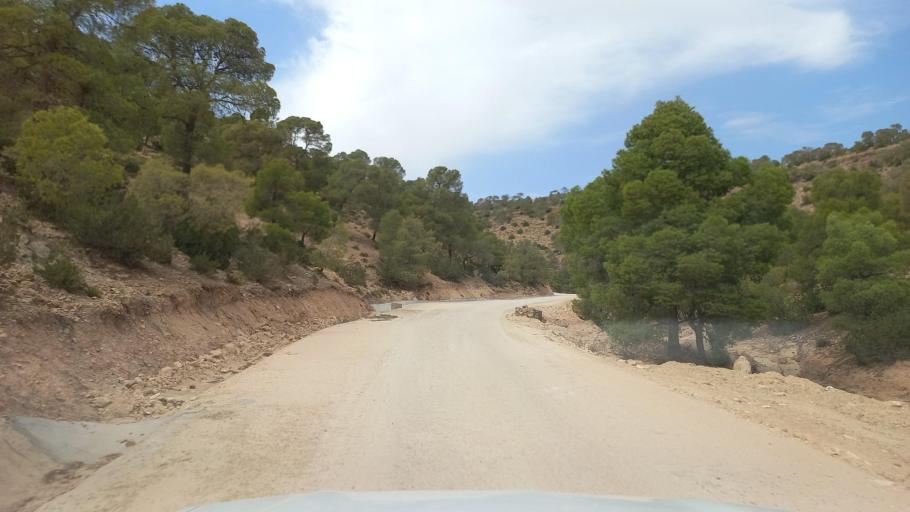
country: TN
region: Al Qasrayn
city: Kasserine
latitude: 35.3752
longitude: 8.8875
